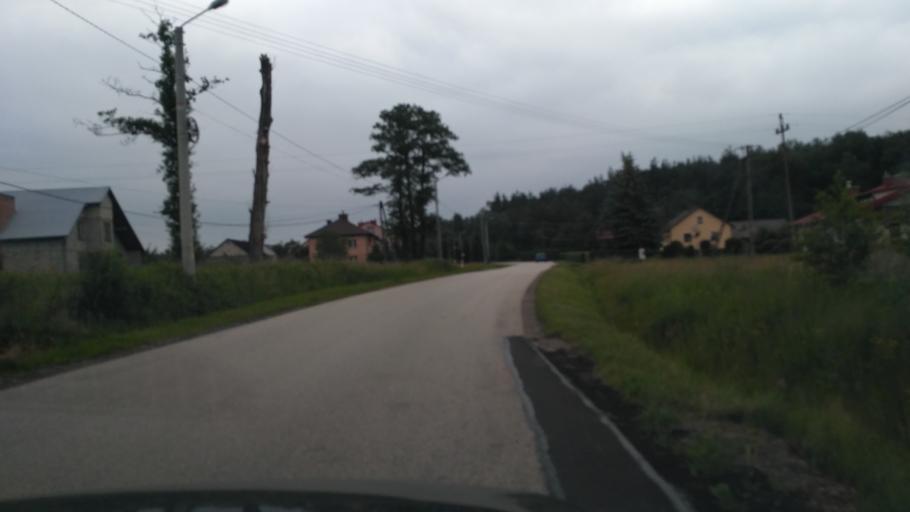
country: PL
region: Subcarpathian Voivodeship
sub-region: Powiat ropczycko-sedziszowski
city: Sedziszow Malopolski
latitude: 50.1118
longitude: 21.6725
